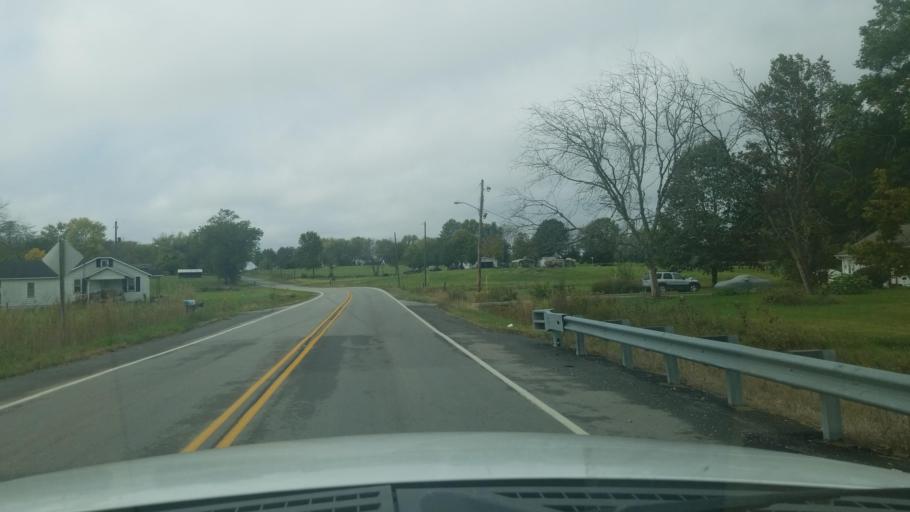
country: US
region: Illinois
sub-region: Saline County
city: Harrisburg
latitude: 37.8411
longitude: -88.6181
